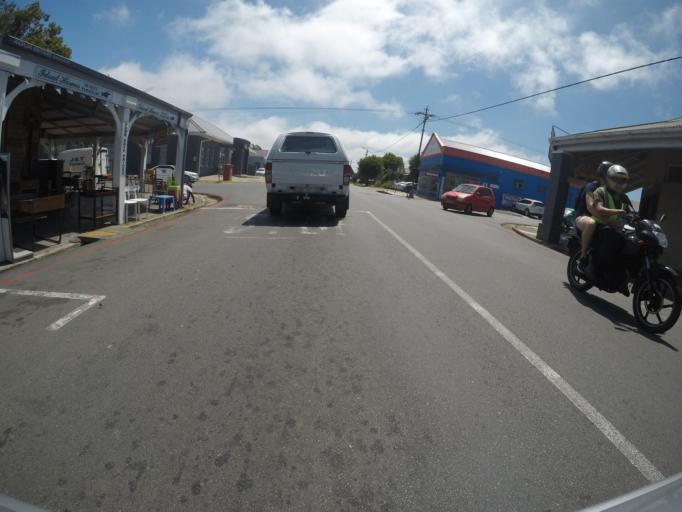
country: ZA
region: Eastern Cape
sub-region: Buffalo City Metropolitan Municipality
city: East London
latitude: -32.9788
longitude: 27.9026
